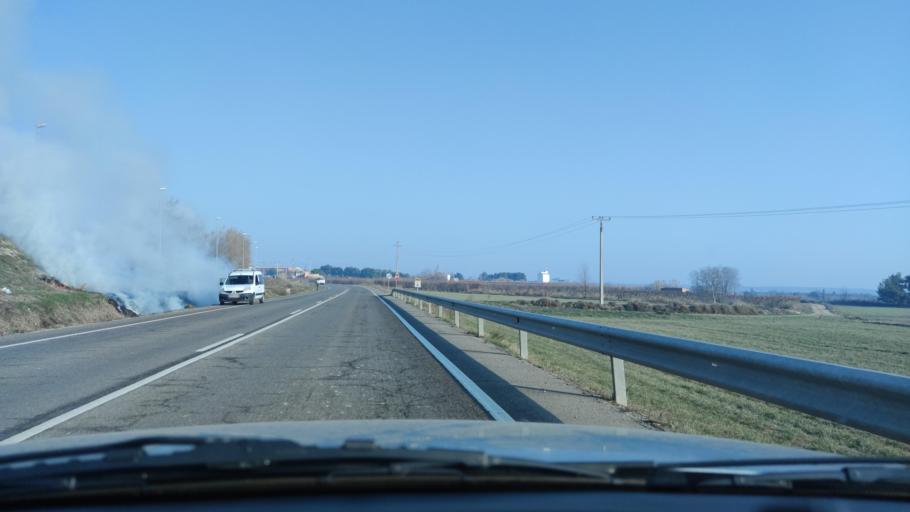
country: ES
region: Catalonia
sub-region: Provincia de Lleida
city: Torrefarrera
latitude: 41.6798
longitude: 0.6314
